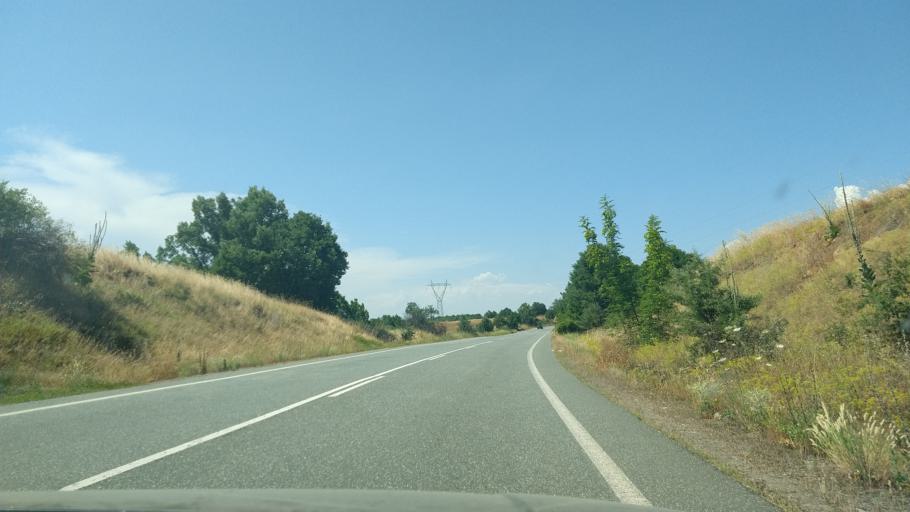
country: GR
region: West Macedonia
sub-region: Nomos Grevenon
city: Grevena
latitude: 40.0597
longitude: 21.4675
